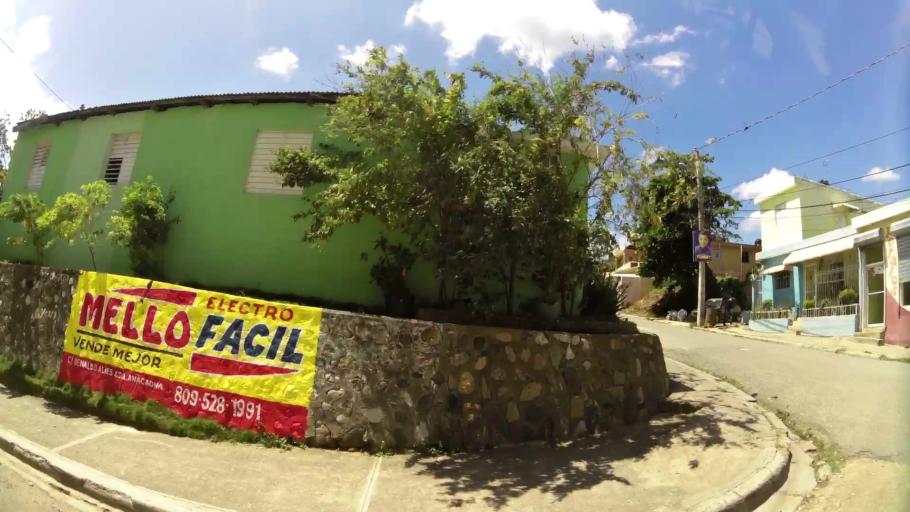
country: DO
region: San Cristobal
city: San Cristobal
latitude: 18.4041
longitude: -70.1094
